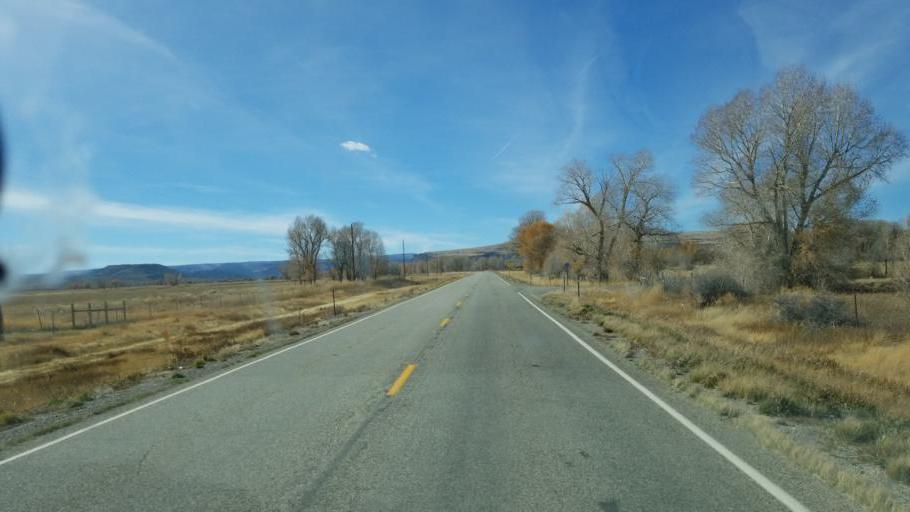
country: US
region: Colorado
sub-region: Conejos County
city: Conejos
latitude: 37.0644
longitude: -106.0688
